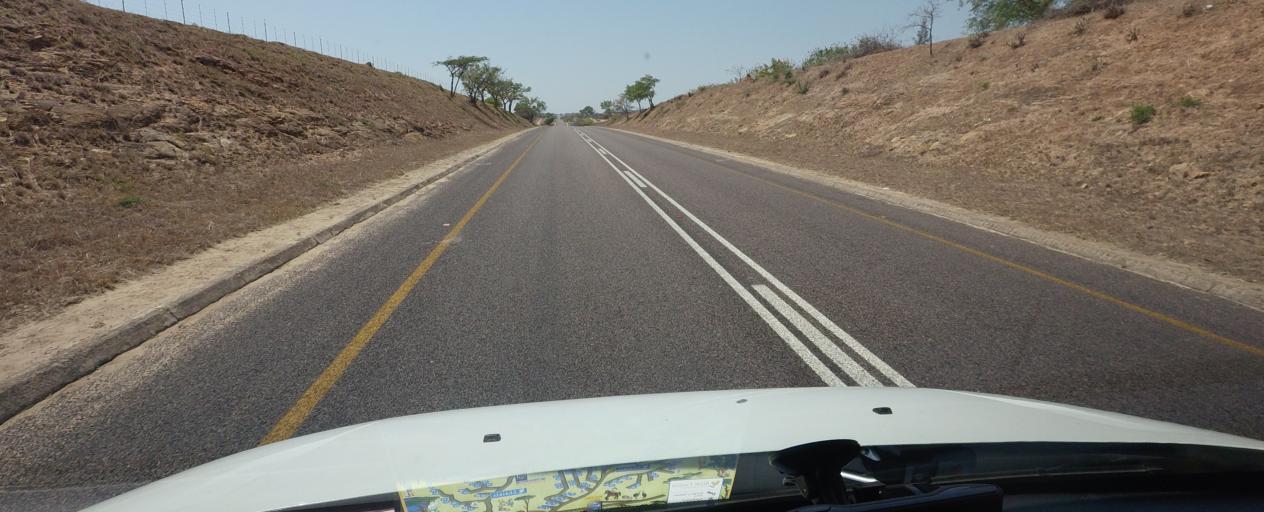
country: ZA
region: Limpopo
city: Thulamahashi
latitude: -24.5684
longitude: 31.0780
